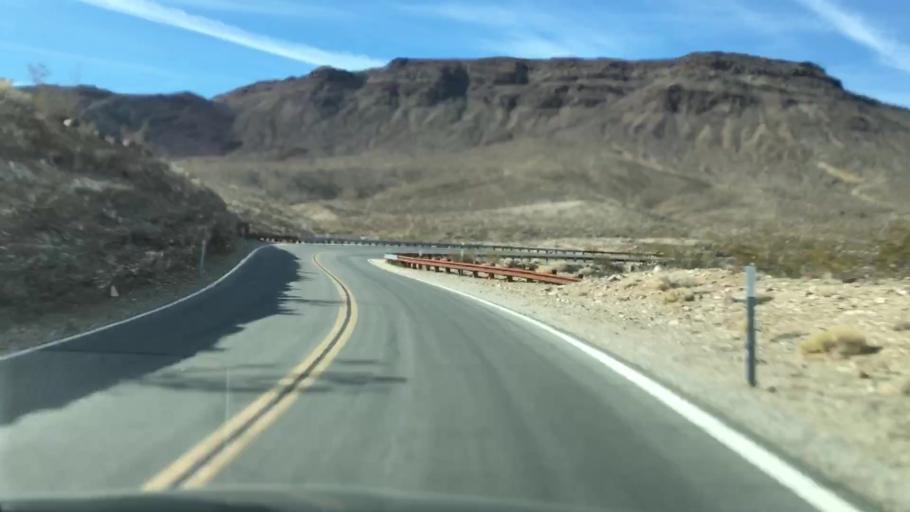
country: US
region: California
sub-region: Inyo County
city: Lone Pine
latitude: 36.3591
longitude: -117.5769
